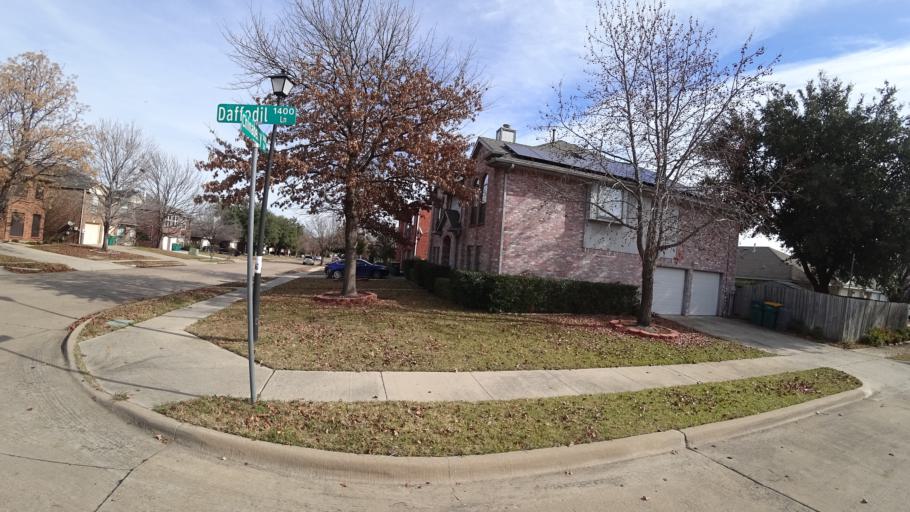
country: US
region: Texas
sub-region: Denton County
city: Highland Village
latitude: 33.0691
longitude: -97.0349
